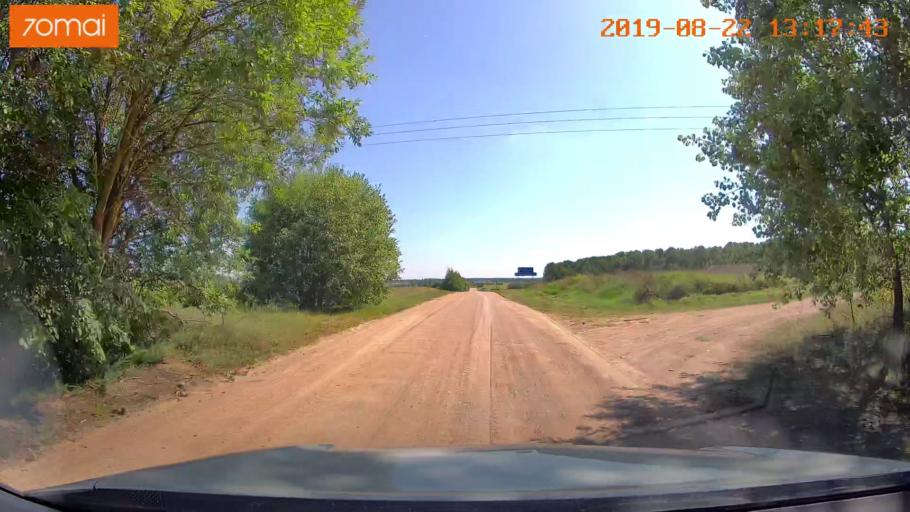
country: BY
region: Minsk
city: Prawdzinski
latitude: 53.2460
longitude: 27.9266
